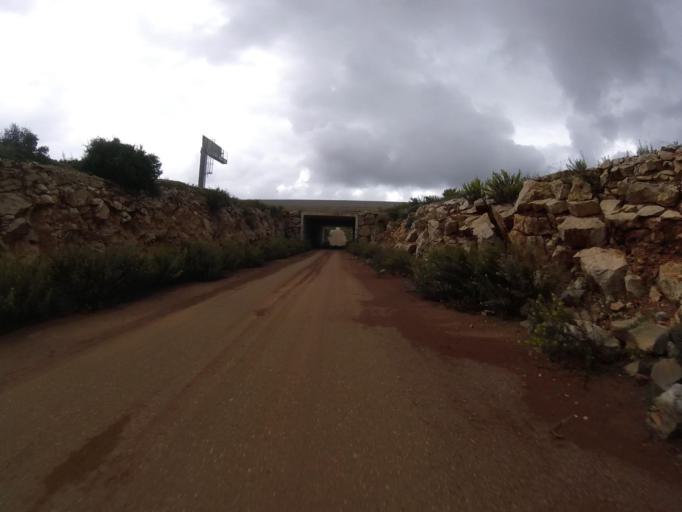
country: ES
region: Valencia
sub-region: Provincia de Castello
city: Benlloch
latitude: 40.2019
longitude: 0.0681
